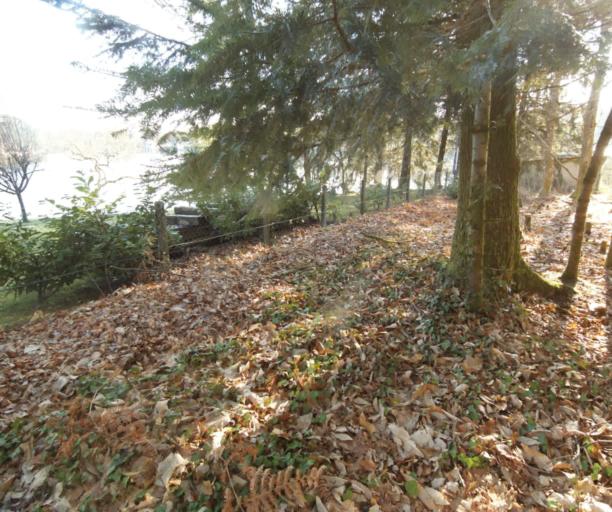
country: FR
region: Limousin
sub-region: Departement de la Correze
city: Correze
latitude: 45.3249
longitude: 1.8735
